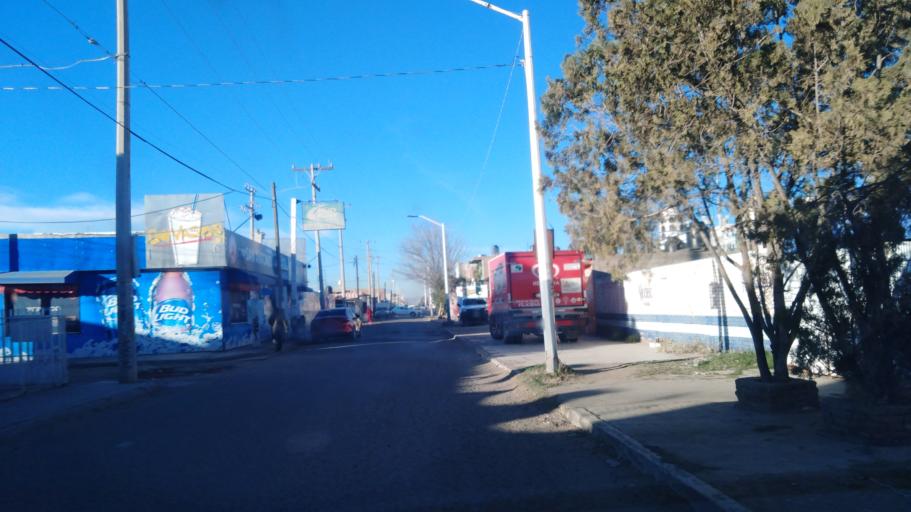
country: MX
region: Durango
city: Victoria de Durango
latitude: 24.0561
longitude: -104.6025
